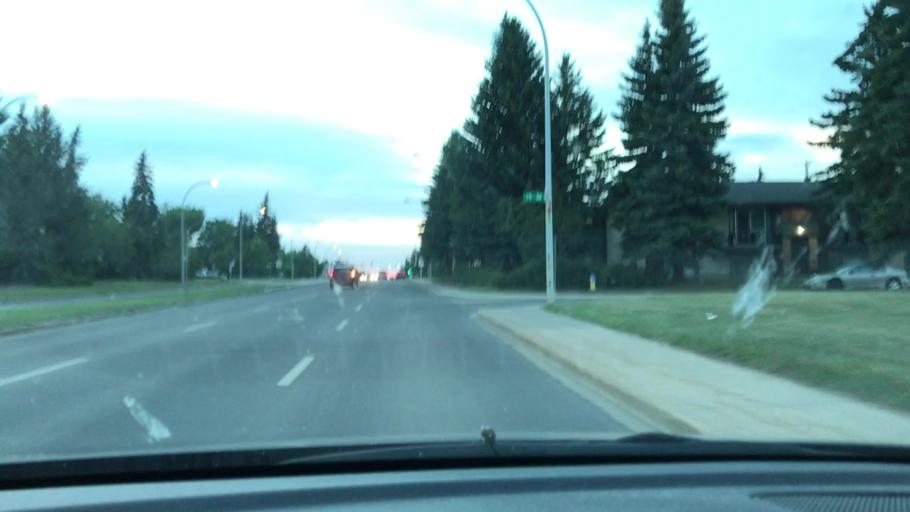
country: CA
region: Alberta
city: Edmonton
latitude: 53.5148
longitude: -113.4428
